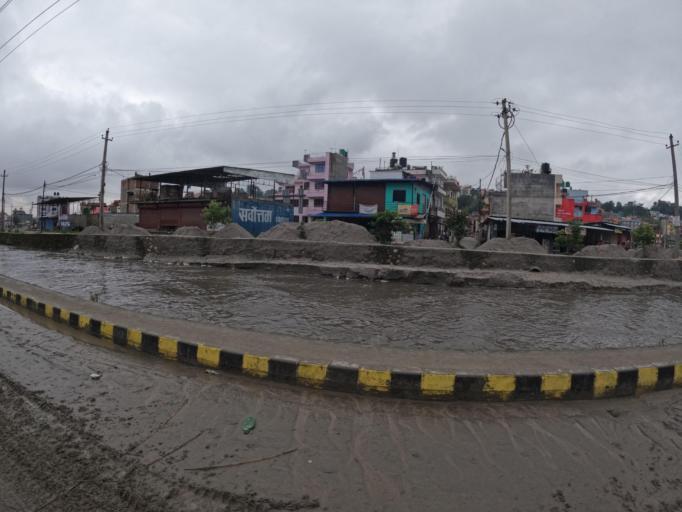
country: NP
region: Central Region
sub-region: Bagmati Zone
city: Kathmandu
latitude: 27.7560
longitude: 85.3173
